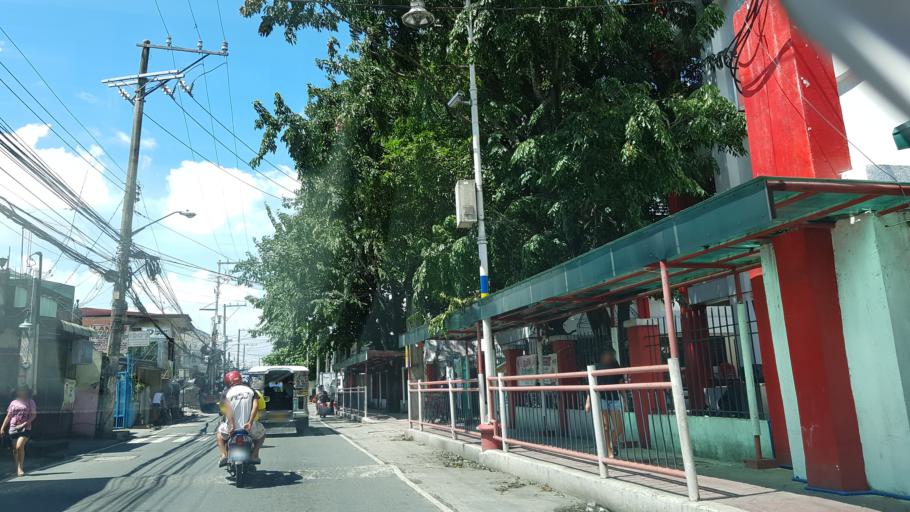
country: PH
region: Calabarzon
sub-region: Province of Rizal
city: Pateros
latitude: 14.5366
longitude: 121.0677
